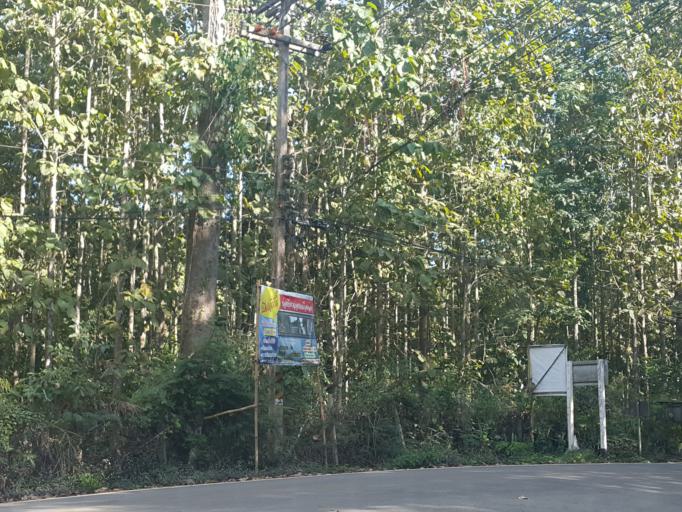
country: TH
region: Chiang Mai
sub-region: Amphoe Chiang Dao
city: Chiang Dao
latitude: 19.3997
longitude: 98.9277
